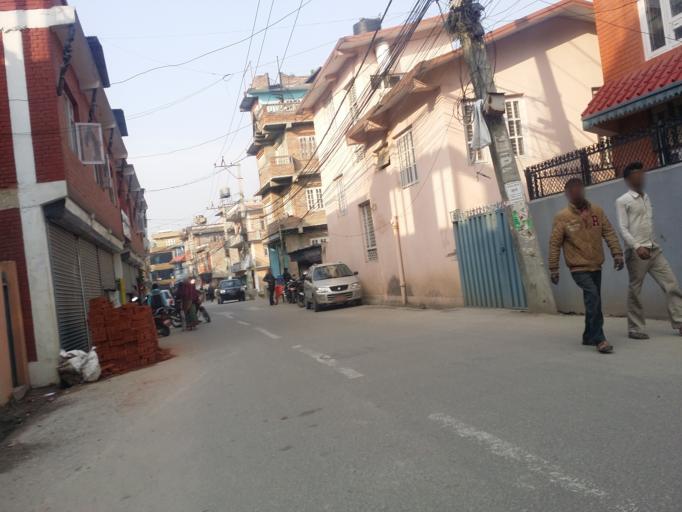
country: NP
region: Central Region
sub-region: Bagmati Zone
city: Kathmandu
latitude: 27.7012
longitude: 85.3465
